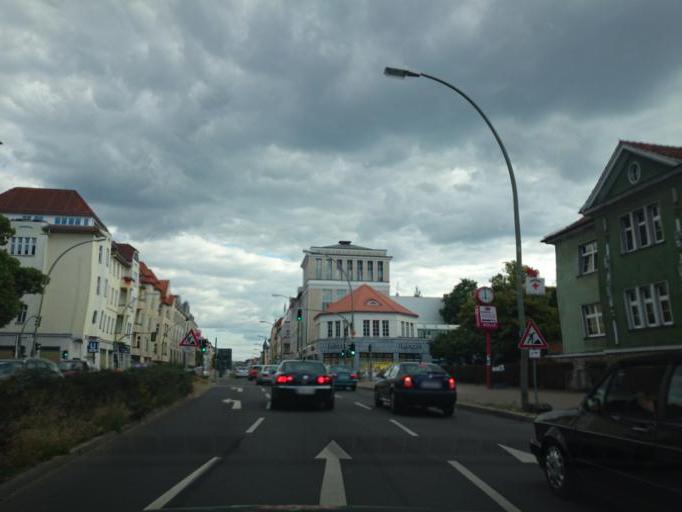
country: DE
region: Berlin
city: Tempelhof Bezirk
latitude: 52.4613
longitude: 13.3849
